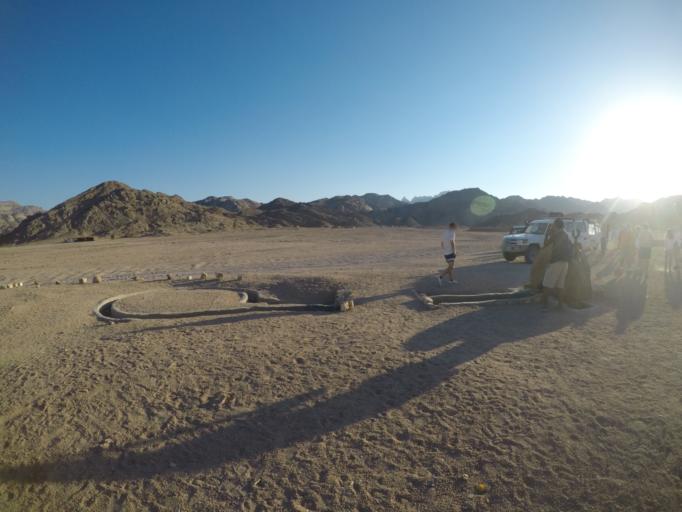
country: EG
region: Red Sea
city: El Gouna
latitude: 27.1509
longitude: 33.5447
